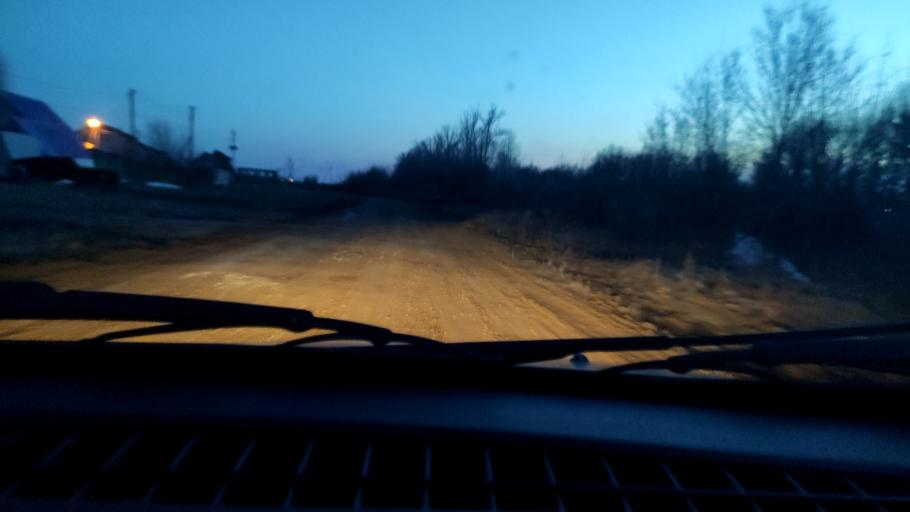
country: RU
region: Bashkortostan
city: Iglino
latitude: 54.7952
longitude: 56.3102
